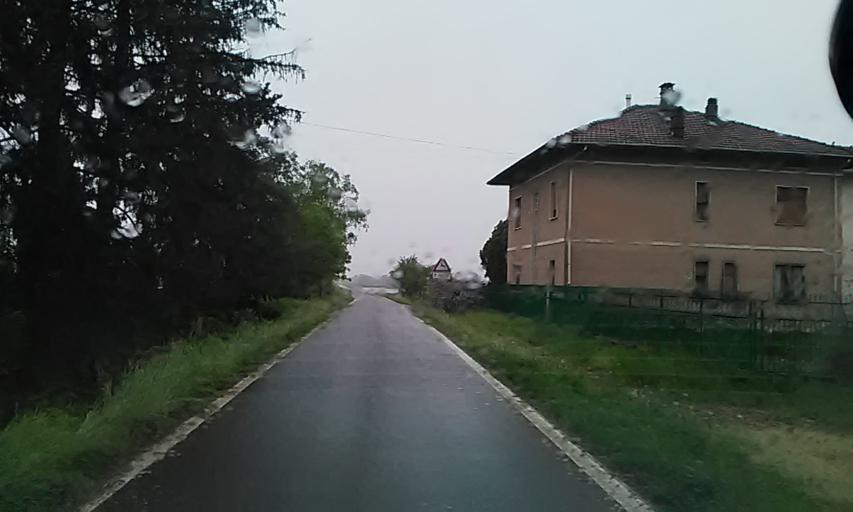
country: IT
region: Piedmont
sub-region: Provincia di Vercelli
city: San Giacomo Vercellese
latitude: 45.4972
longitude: 8.3352
